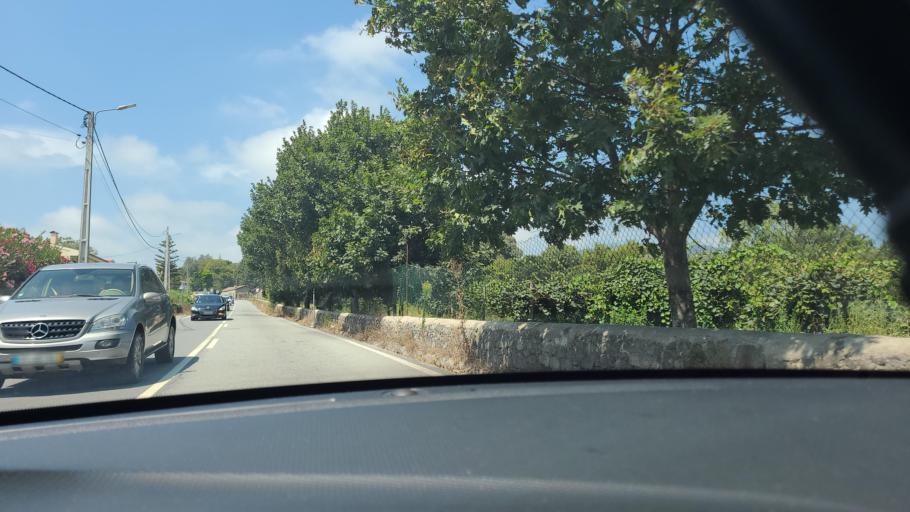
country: PT
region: Braga
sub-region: Amares
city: Amares
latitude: 41.6230
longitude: -8.3377
